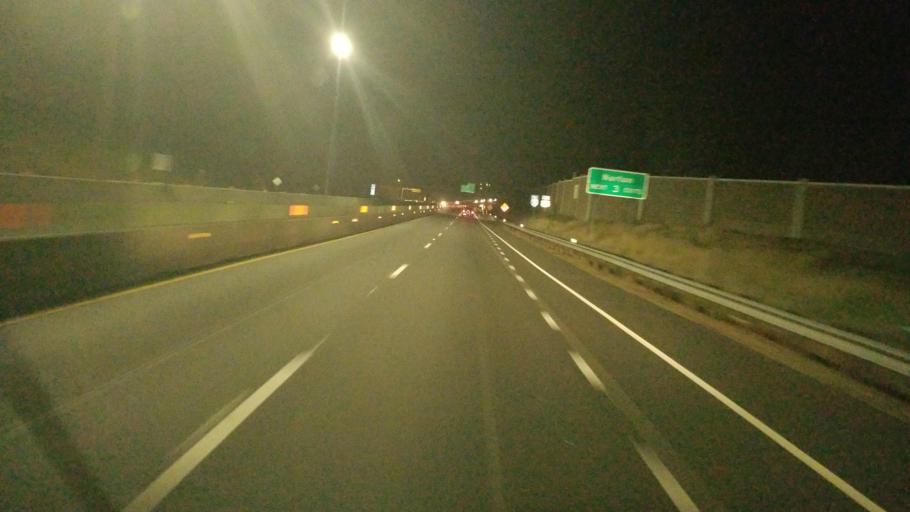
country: US
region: Ohio
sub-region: Summit County
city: Barberton
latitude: 41.0392
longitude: -81.5904
